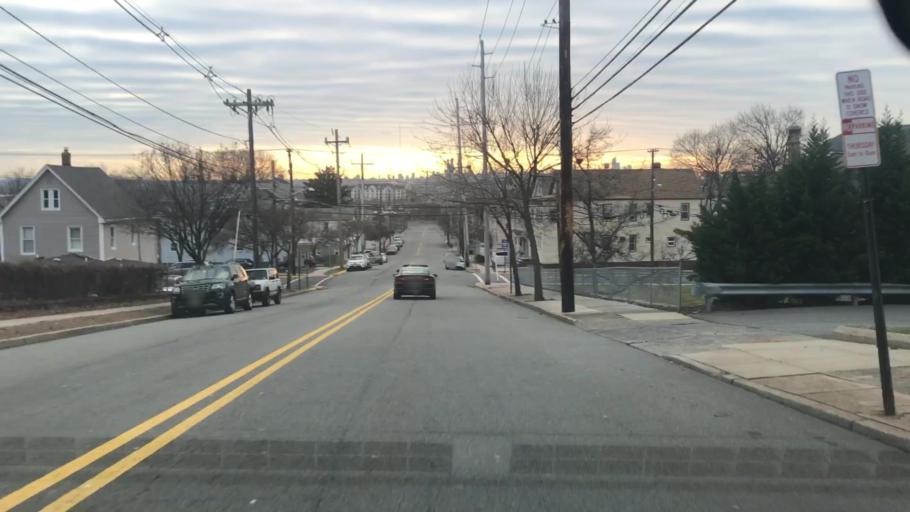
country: US
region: New Jersey
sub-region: Bergen County
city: Carlstadt
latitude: 40.8353
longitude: -74.0920
